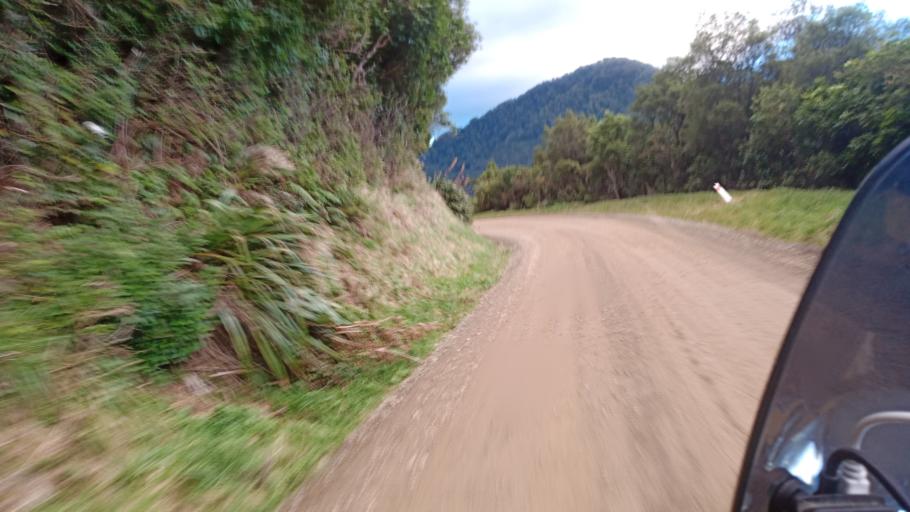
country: NZ
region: Hawke's Bay
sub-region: Wairoa District
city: Wairoa
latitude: -38.7266
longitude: 177.0658
